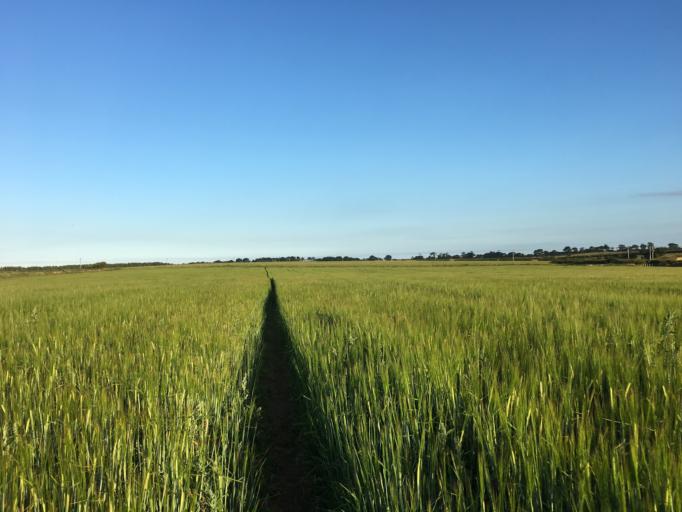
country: GB
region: England
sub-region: Northumberland
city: North Sunderland
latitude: 55.5858
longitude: -1.6770
